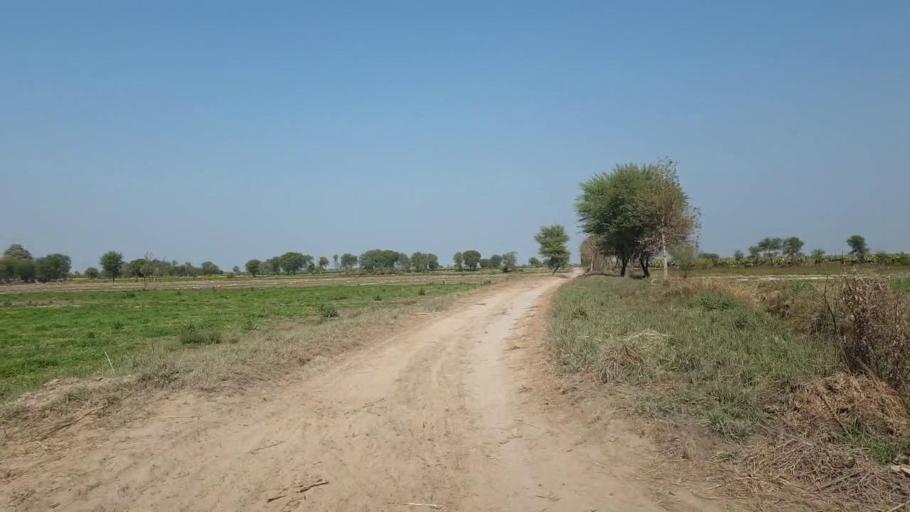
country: PK
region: Sindh
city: Hala
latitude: 25.9589
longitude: 68.4338
